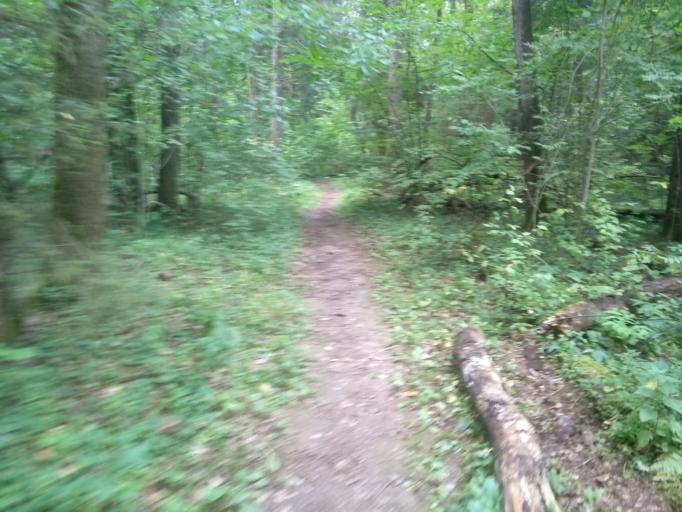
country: RU
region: Moskovskaya
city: Dedovsk
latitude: 55.8730
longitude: 37.0924
